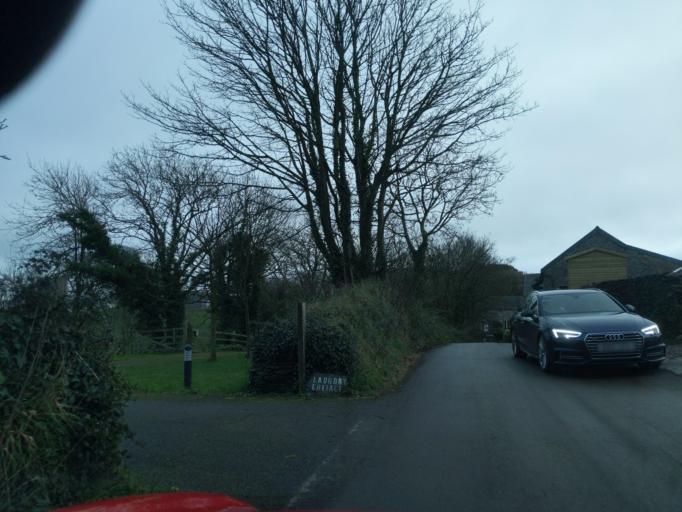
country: GB
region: England
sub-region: Devon
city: Wembury
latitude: 50.3273
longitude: -4.0880
